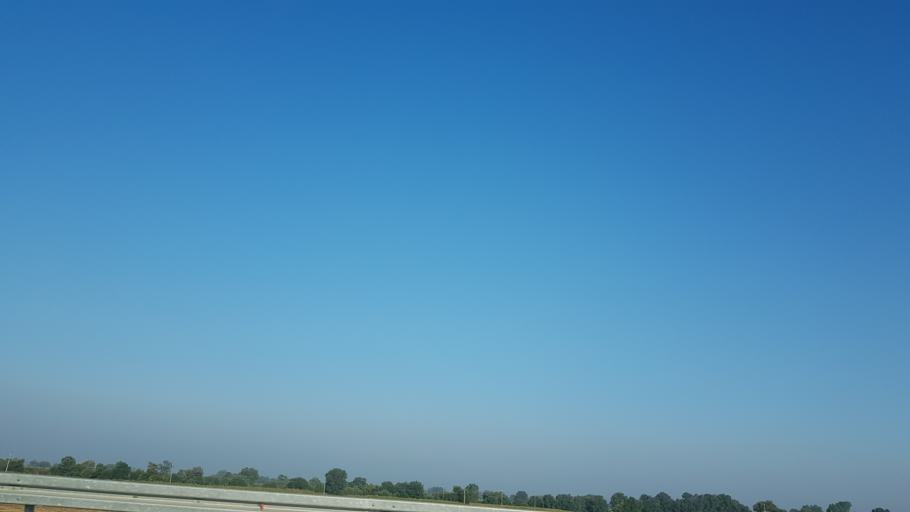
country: TR
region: Bursa
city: Tatkavakli
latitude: 40.1171
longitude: 28.2783
